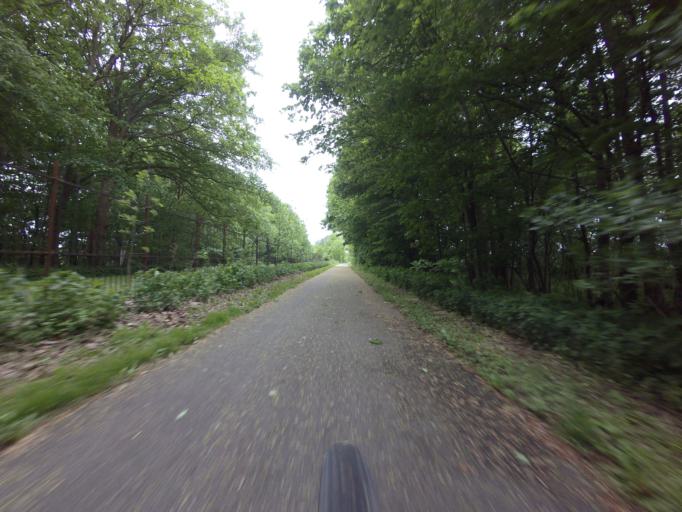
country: DK
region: Zealand
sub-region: Slagelse Kommune
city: Skaelskor
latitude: 55.2510
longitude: 11.3581
